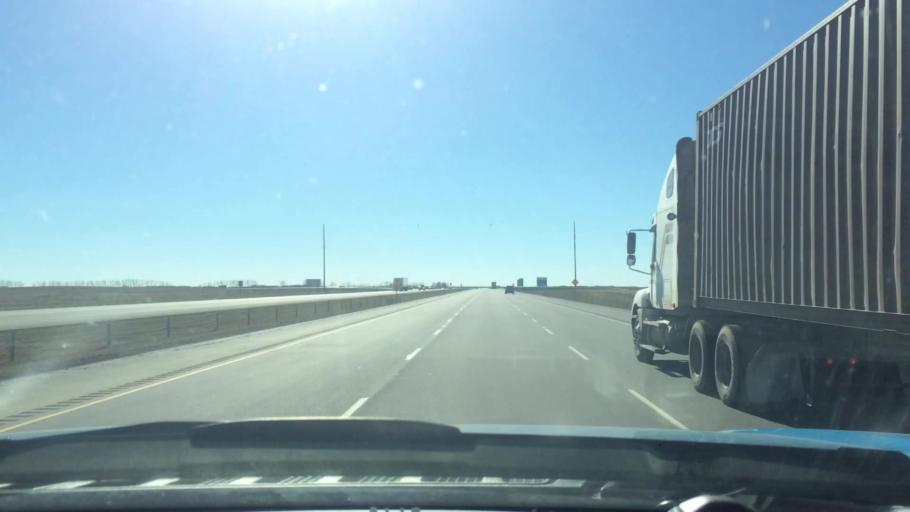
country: CA
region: Alberta
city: Crossfield
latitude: 51.3979
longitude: -114.0021
